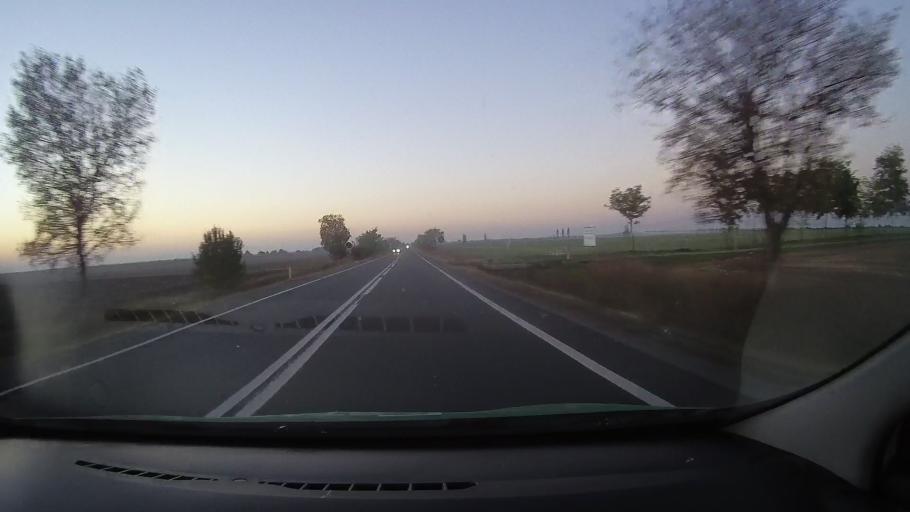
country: RO
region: Bihor
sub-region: Comuna Tarcea
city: Tarcea
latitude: 47.4805
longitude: 22.1628
